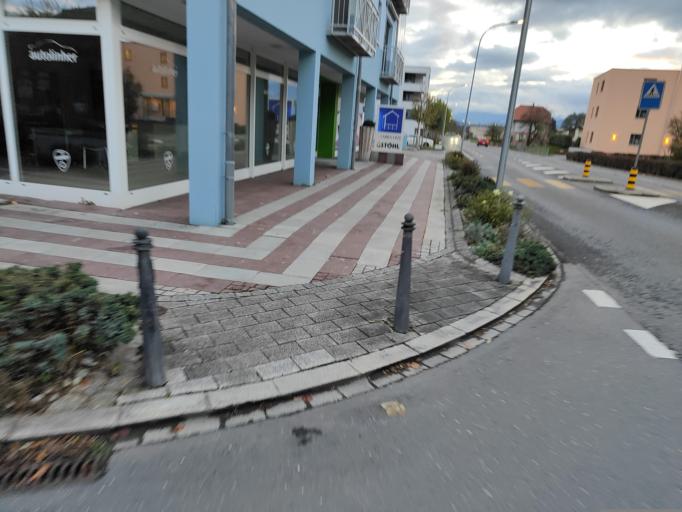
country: LI
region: Eschen
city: Eschen
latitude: 47.2104
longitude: 9.5277
